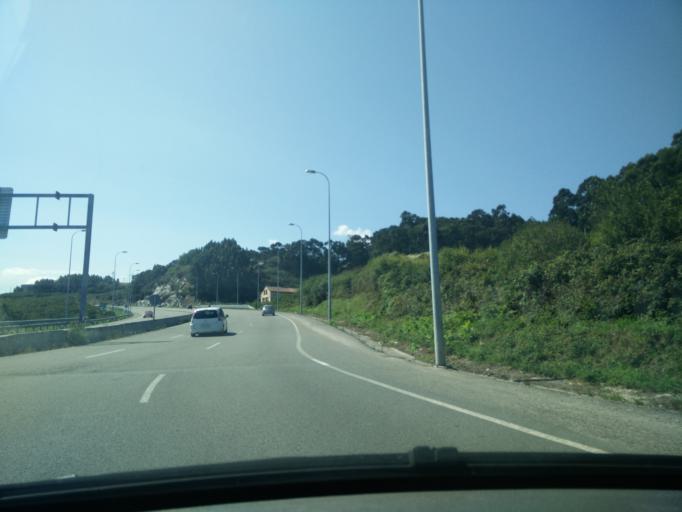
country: ES
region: Galicia
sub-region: Provincia da Coruna
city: A Coruna
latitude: 43.3665
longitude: -8.4307
